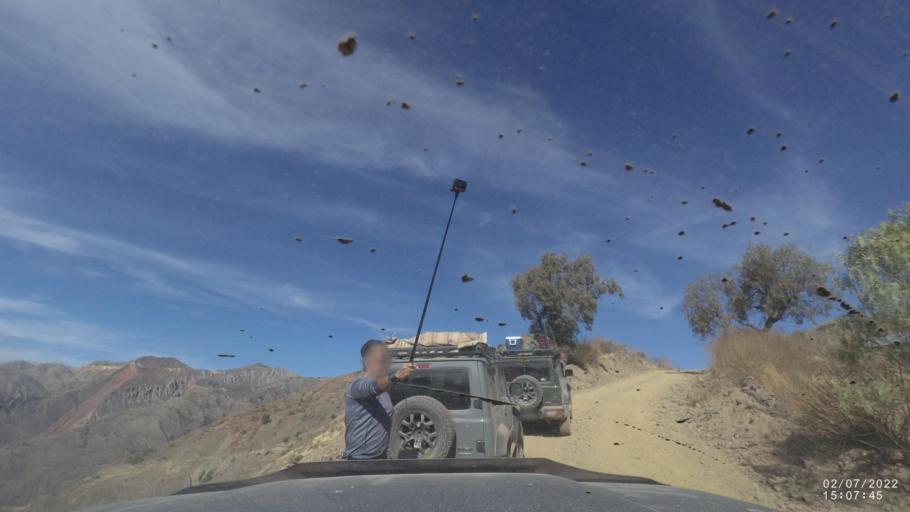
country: BO
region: Cochabamba
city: Irpa Irpa
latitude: -17.8602
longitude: -66.4382
